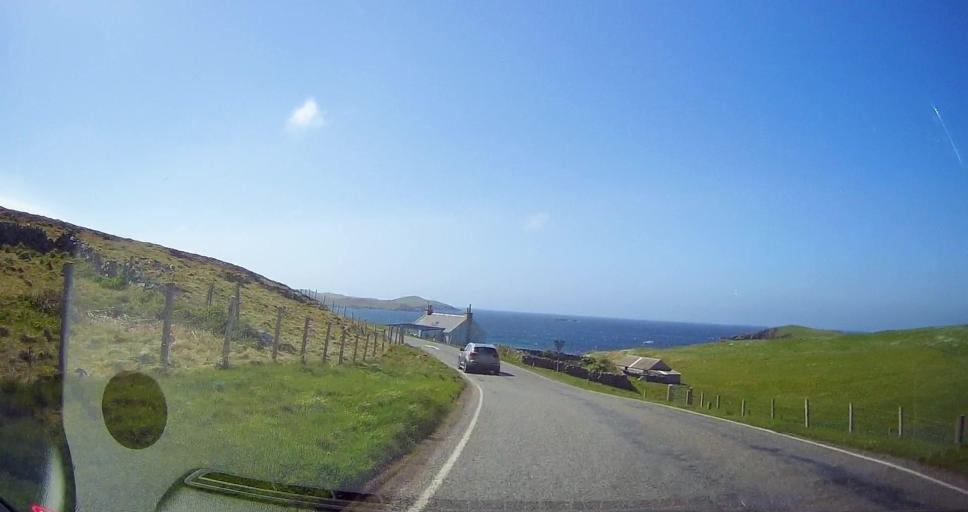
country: GB
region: Scotland
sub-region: Shetland Islands
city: Sandwick
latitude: 60.1039
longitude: -1.3249
